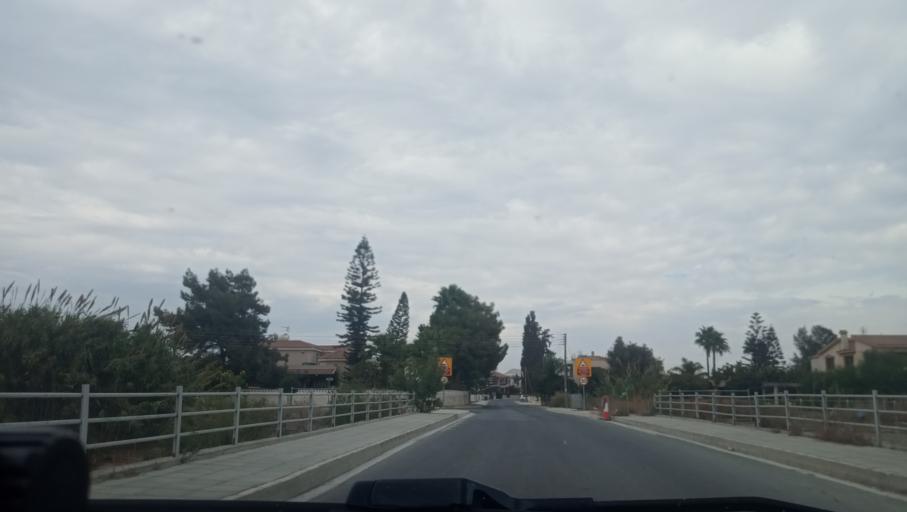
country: CY
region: Larnaka
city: Livadia
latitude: 34.9502
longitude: 33.6291
